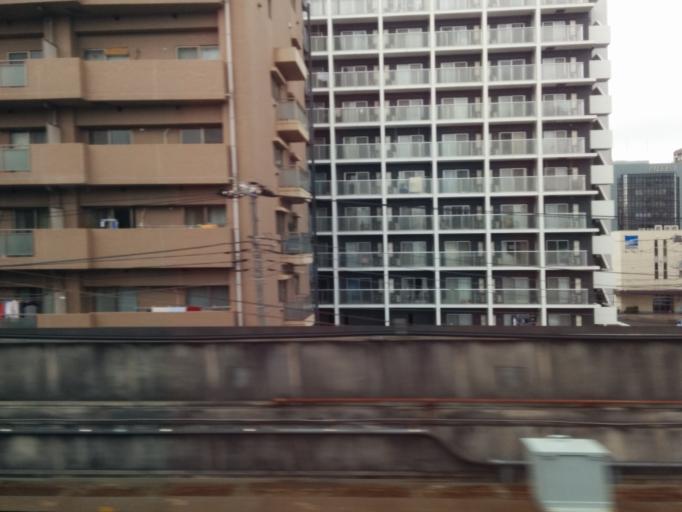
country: JP
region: Kanagawa
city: Yokohama
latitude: 35.5053
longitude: 139.6146
